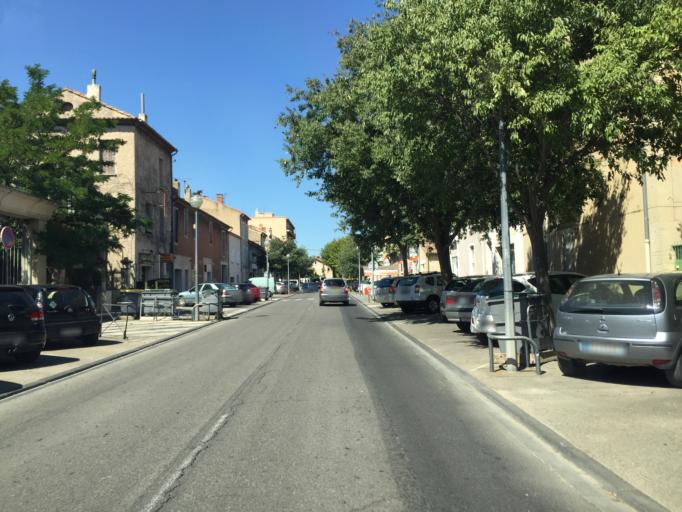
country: FR
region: Provence-Alpes-Cote d'Azur
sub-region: Departement du Vaucluse
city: Carpentras
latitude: 44.0527
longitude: 5.0431
